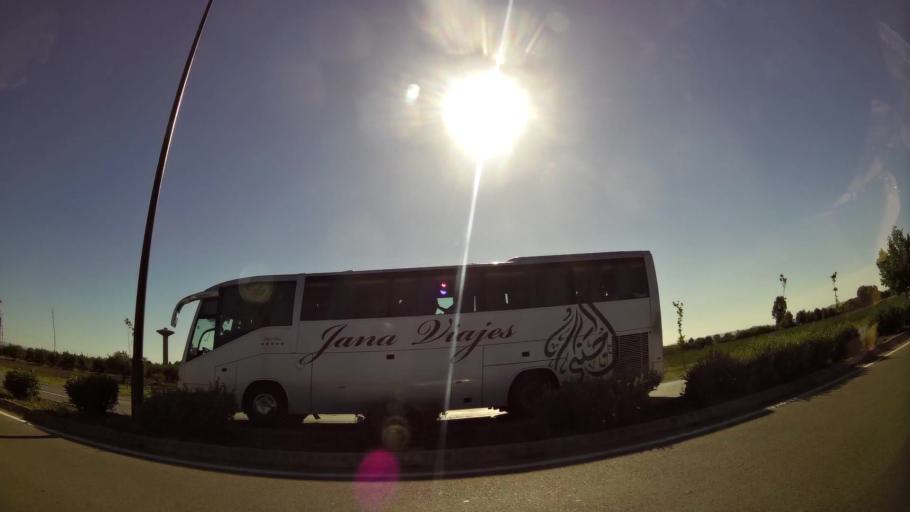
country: MA
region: Fes-Boulemane
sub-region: Fes
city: Fes
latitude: 33.9950
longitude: -5.0243
